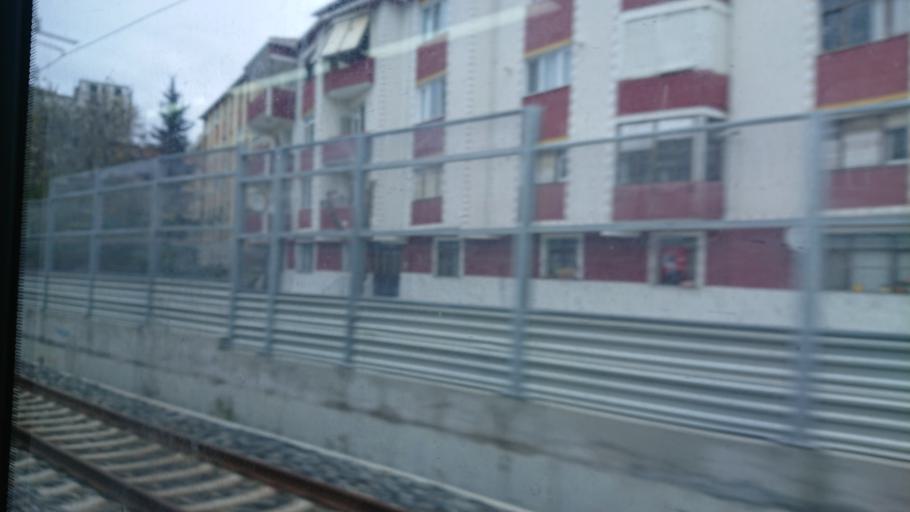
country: TR
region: Istanbul
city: Mahmutbey
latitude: 40.9949
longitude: 28.7684
